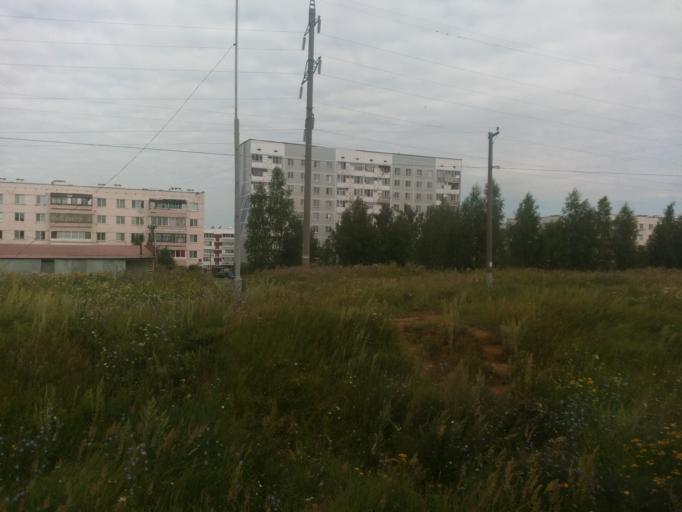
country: RU
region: Tatarstan
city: Mendeleyevsk
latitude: 55.8837
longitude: 52.3106
